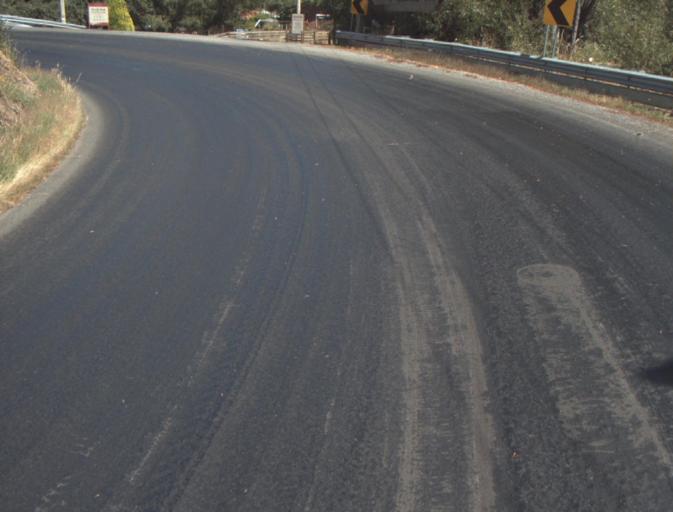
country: AU
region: Tasmania
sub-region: Dorset
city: Scottsdale
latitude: -41.3106
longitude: 147.3678
